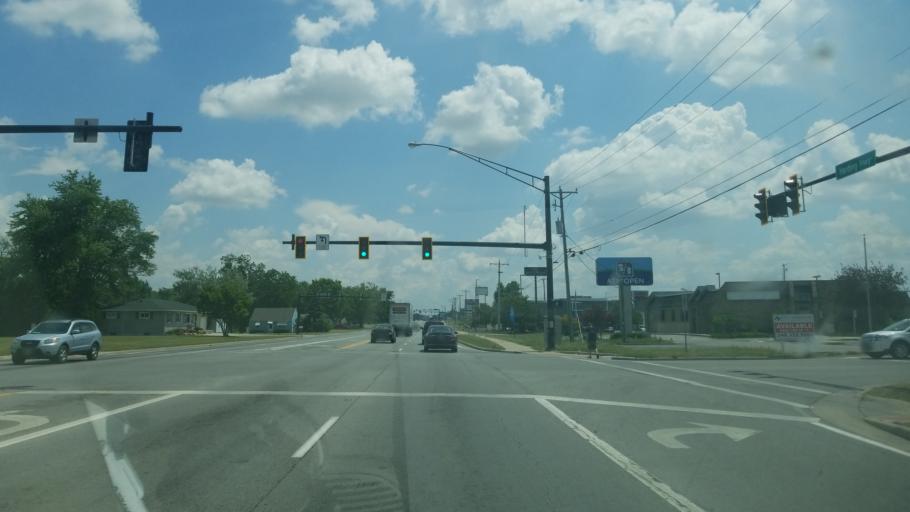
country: US
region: Ohio
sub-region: Allen County
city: Lima
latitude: 40.7306
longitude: -84.0672
